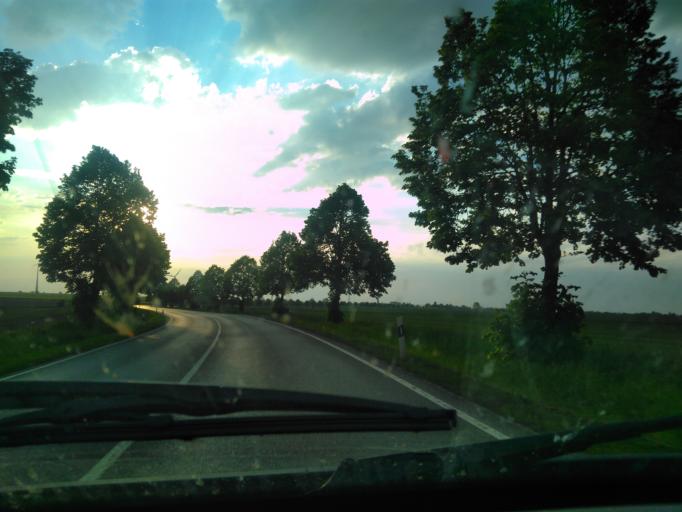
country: DE
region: Saxony-Anhalt
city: Osterfeld
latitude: 51.0963
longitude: 11.9465
